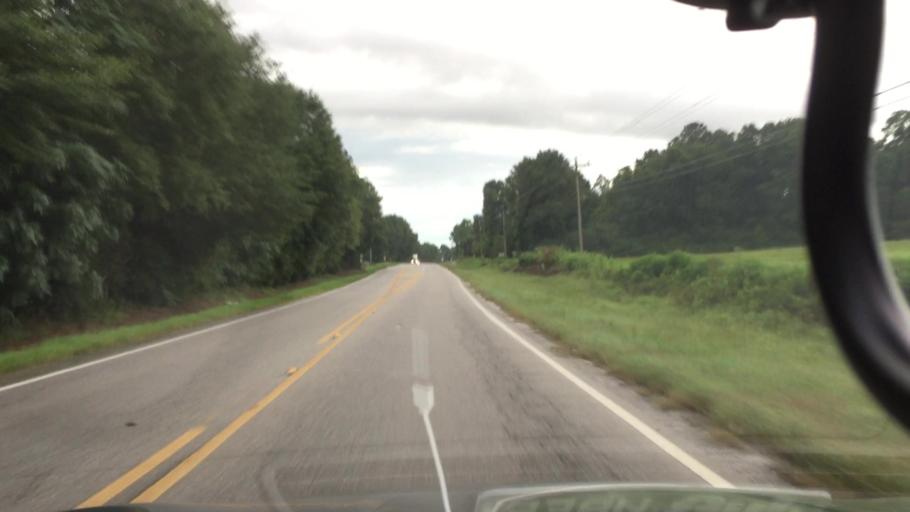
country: US
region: Alabama
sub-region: Pike County
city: Troy
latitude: 31.7331
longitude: -85.9575
